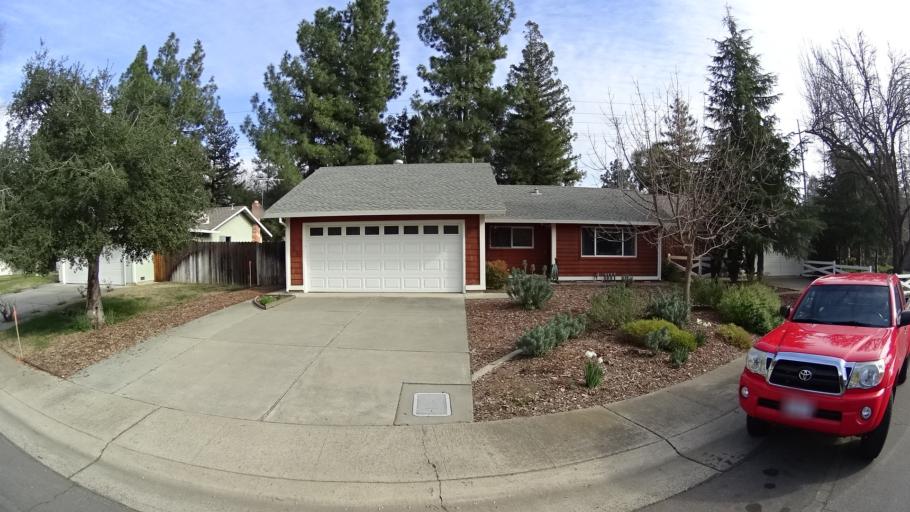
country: US
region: California
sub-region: Yolo County
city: Davis
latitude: 38.5445
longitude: -121.7140
